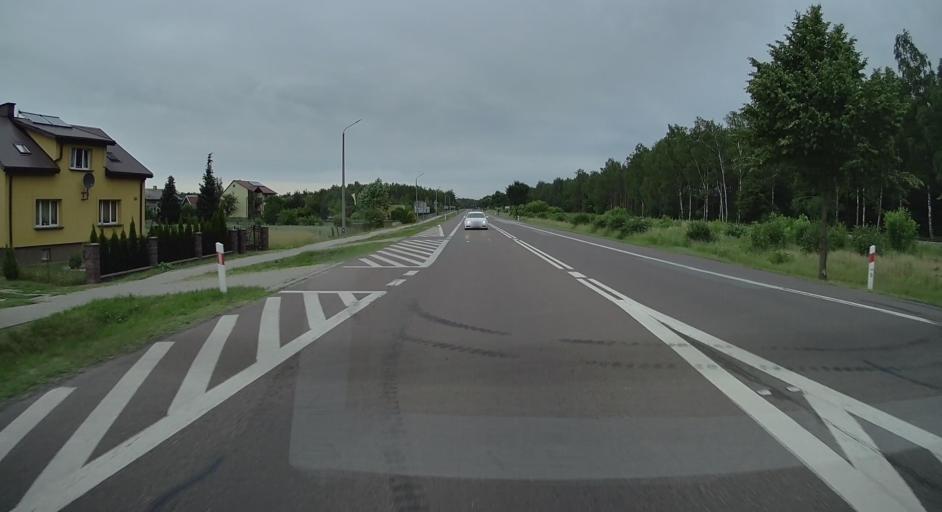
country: PL
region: Lublin Voivodeship
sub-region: Powiat bialski
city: Terespol
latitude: 52.0410
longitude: 23.5202
